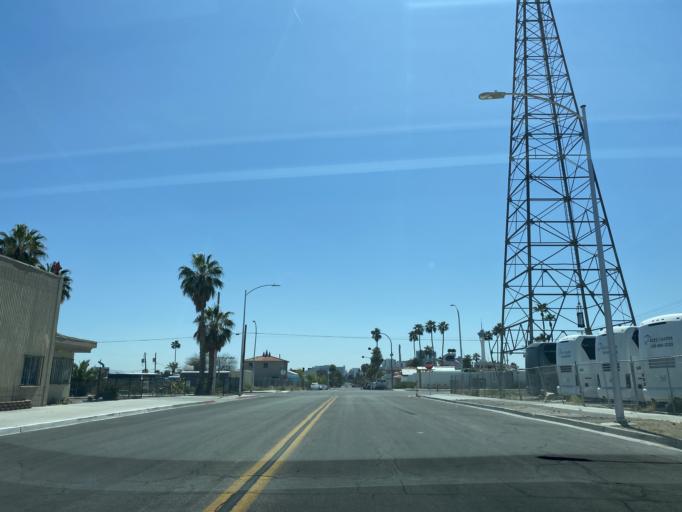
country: US
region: Nevada
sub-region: Clark County
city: Las Vegas
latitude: 36.1680
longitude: -115.1327
